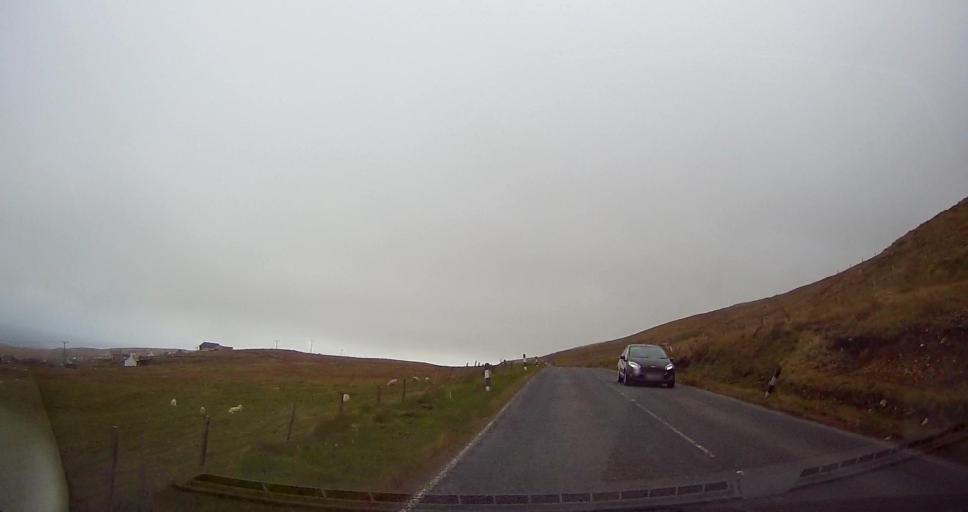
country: GB
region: Scotland
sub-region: Shetland Islands
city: Sandwick
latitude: 59.9712
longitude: -1.2785
